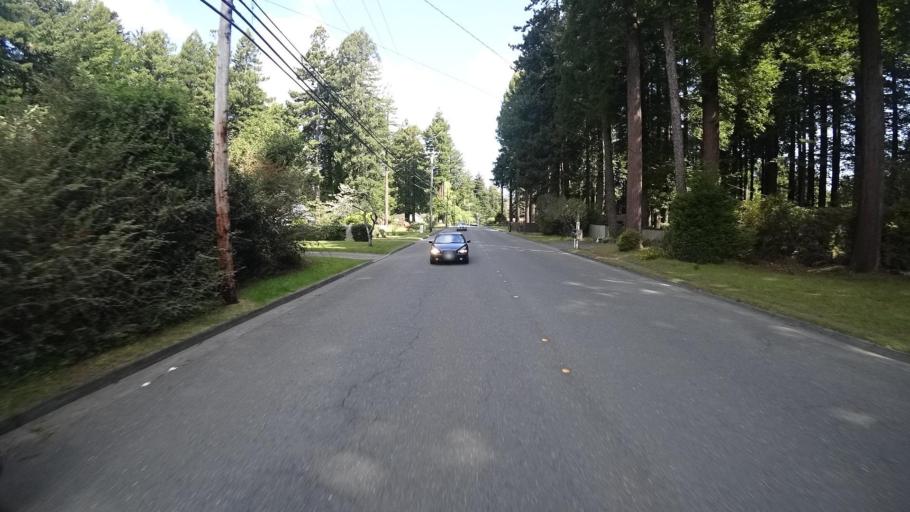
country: US
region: California
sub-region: Humboldt County
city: Cutten
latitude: 40.7630
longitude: -124.1546
